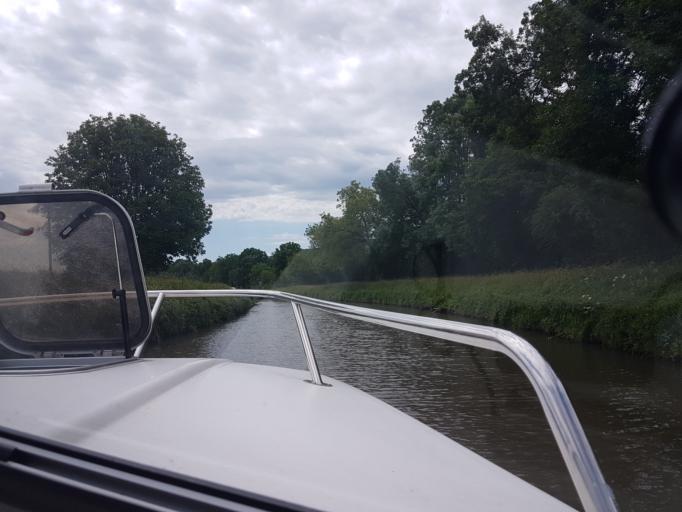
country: FR
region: Bourgogne
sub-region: Departement de la Nievre
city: Clamecy
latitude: 47.4949
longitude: 3.5101
